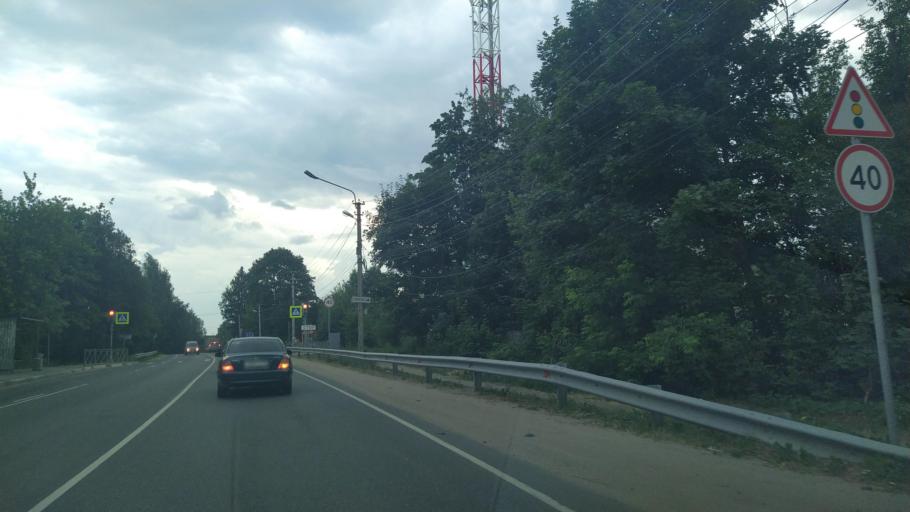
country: RU
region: Leningrad
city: Toksovo
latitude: 60.1613
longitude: 30.5365
